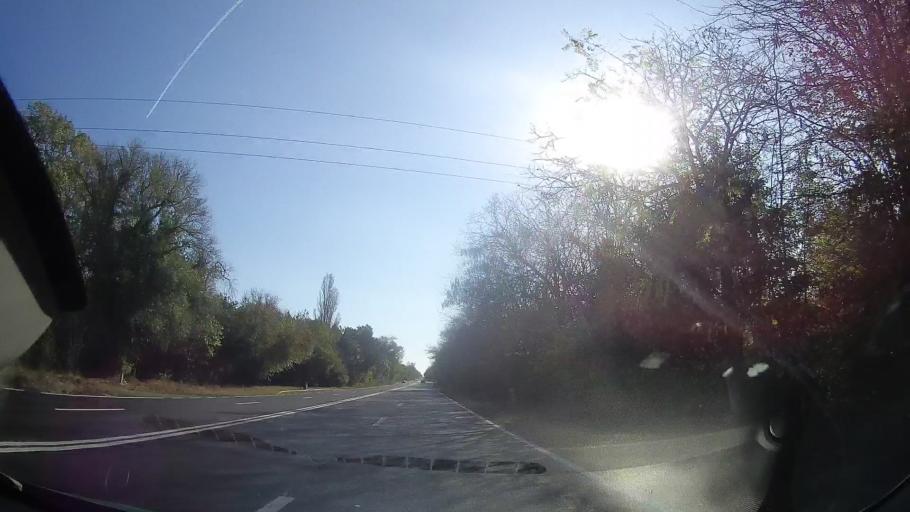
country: RO
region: Constanta
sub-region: Comuna Douazeci si Trei August
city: Dulcesti
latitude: 43.8777
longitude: 28.5738
